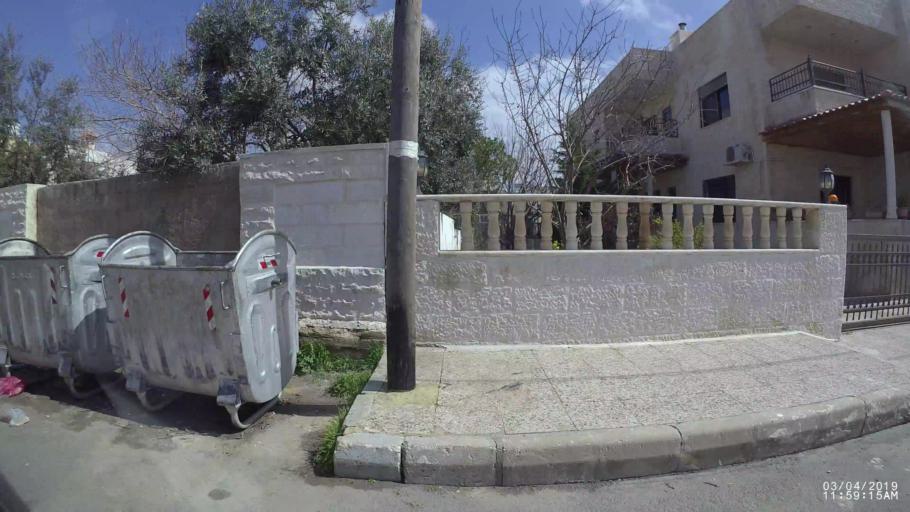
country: JO
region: Amman
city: Wadi as Sir
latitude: 31.9607
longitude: 35.8426
